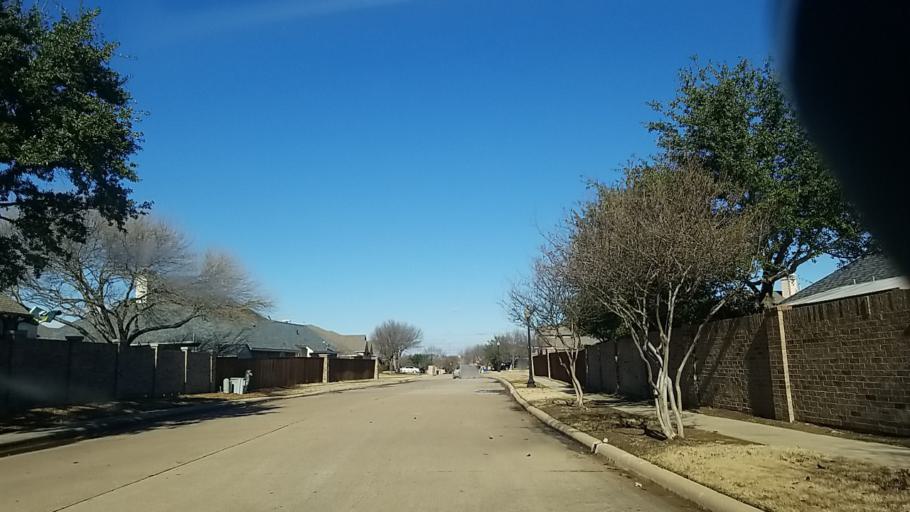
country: US
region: Texas
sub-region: Denton County
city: Corinth
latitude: 33.1594
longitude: -97.0800
